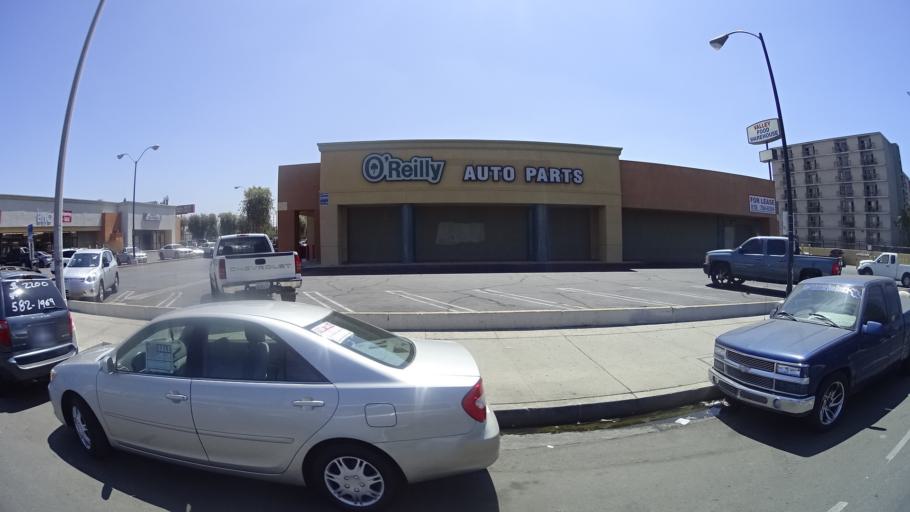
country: US
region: California
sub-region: Los Angeles County
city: Van Nuys
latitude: 34.2346
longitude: -118.4503
